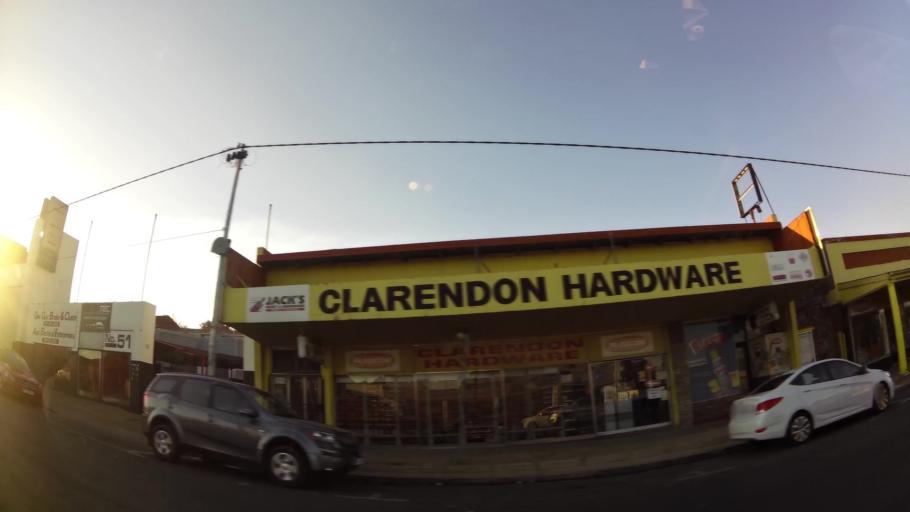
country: ZA
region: Gauteng
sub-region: City of Johannesburg Metropolitan Municipality
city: Roodepoort
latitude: -26.1679
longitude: 27.8981
